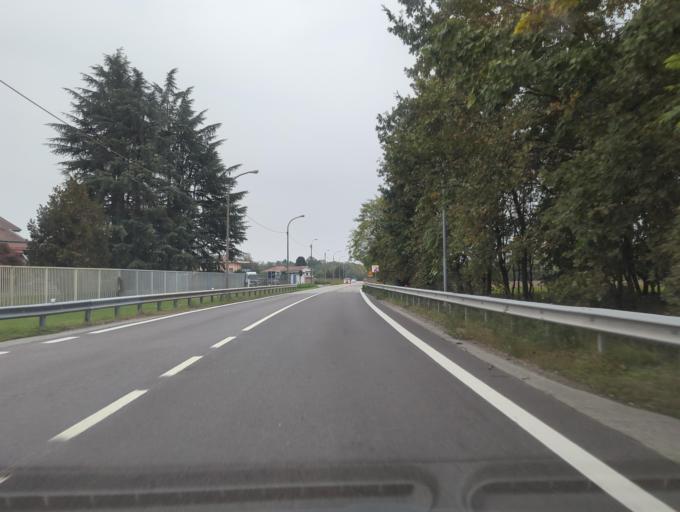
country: IT
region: Piedmont
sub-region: Provincia di Novara
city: Galliate
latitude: 45.4923
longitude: 8.7155
